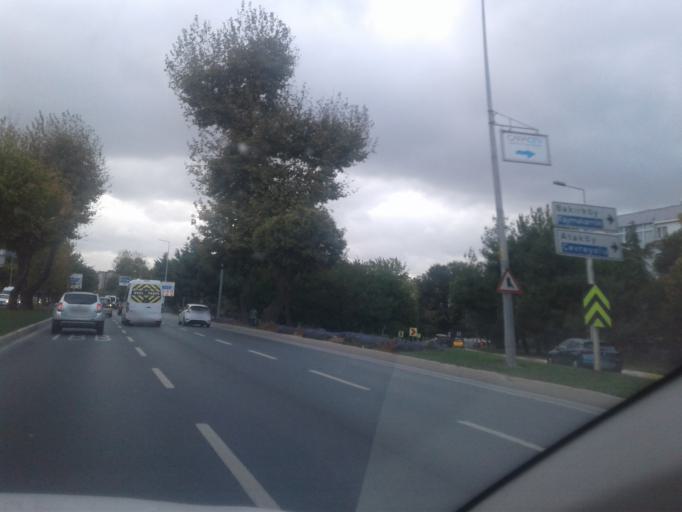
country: TR
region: Istanbul
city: Bahcelievler
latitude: 40.9755
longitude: 28.8679
